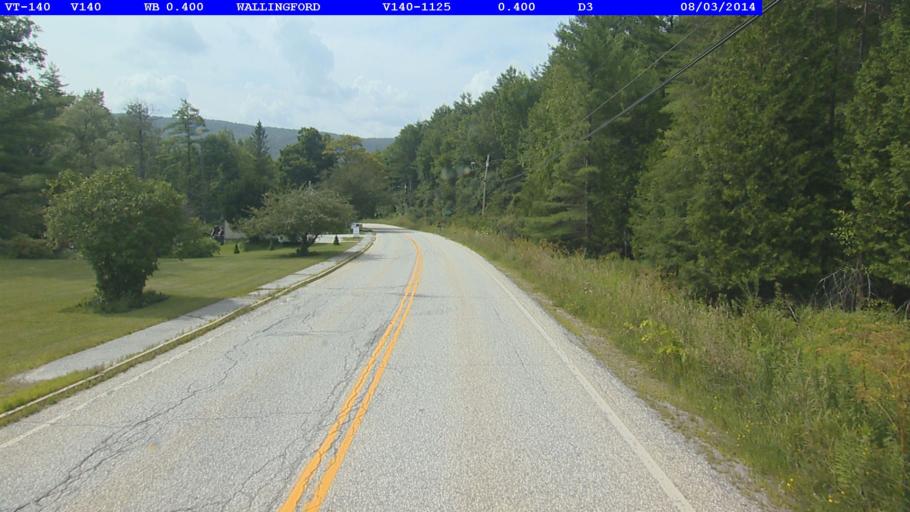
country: US
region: Vermont
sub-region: Rutland County
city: Rutland
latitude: 43.4699
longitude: -72.9698
